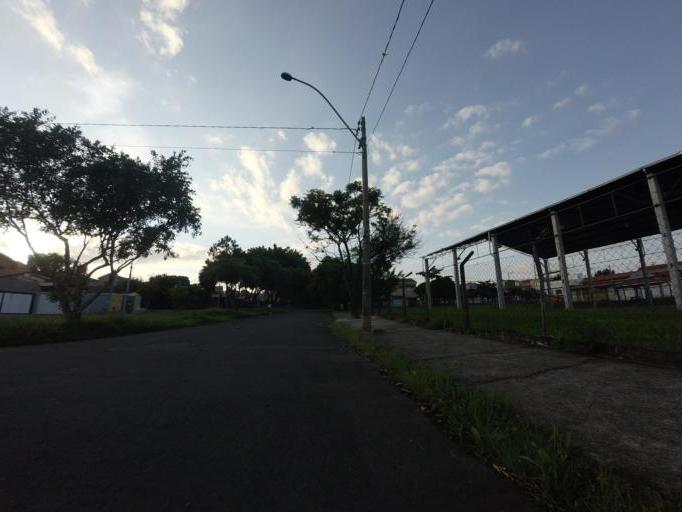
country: BR
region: Sao Paulo
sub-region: Piracicaba
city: Piracicaba
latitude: -22.7605
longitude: -47.6097
